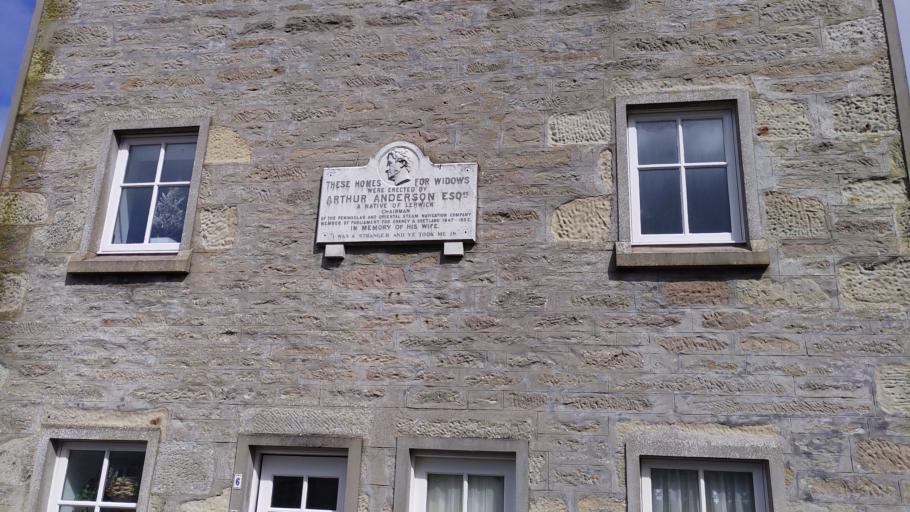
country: GB
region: Scotland
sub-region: Shetland Islands
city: Shetland
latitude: 60.1517
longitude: -1.1358
